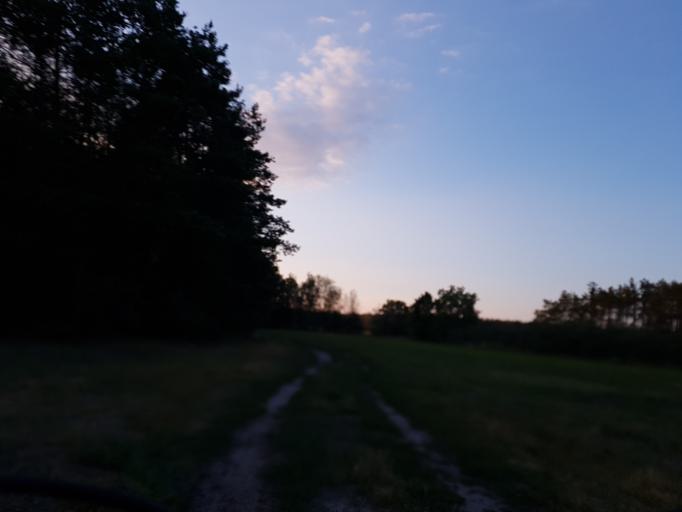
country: DE
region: Brandenburg
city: Trobitz
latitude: 51.6009
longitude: 13.4092
